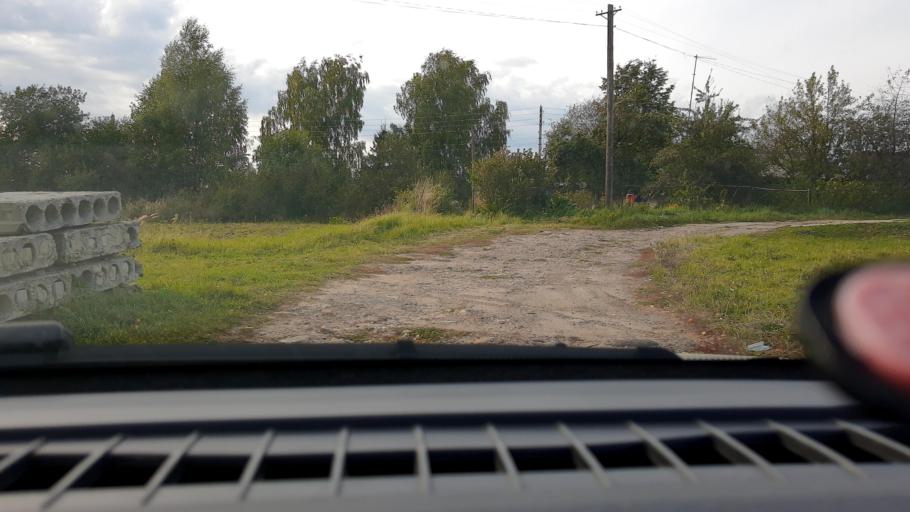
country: RU
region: Nizjnij Novgorod
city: Nizhniy Novgorod
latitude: 56.2073
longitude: 43.9540
